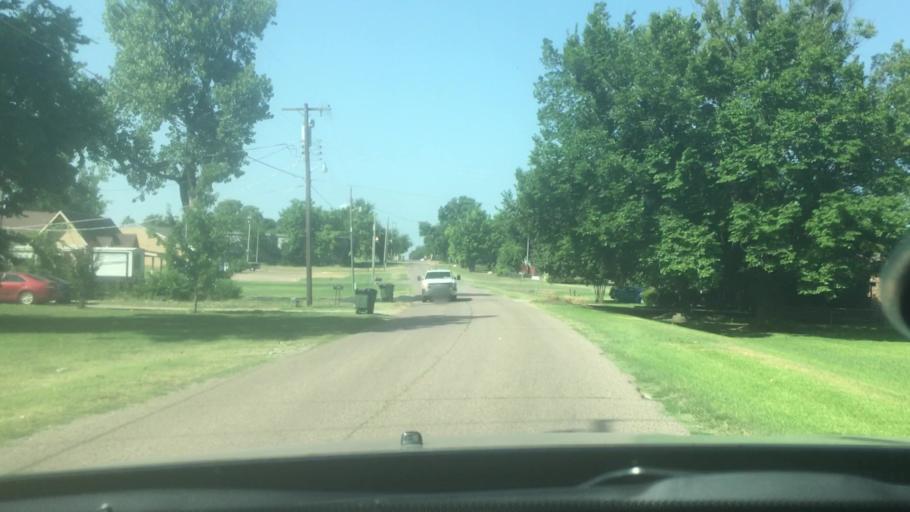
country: US
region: Oklahoma
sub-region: Bryan County
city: Calera
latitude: 33.9383
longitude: -96.4253
